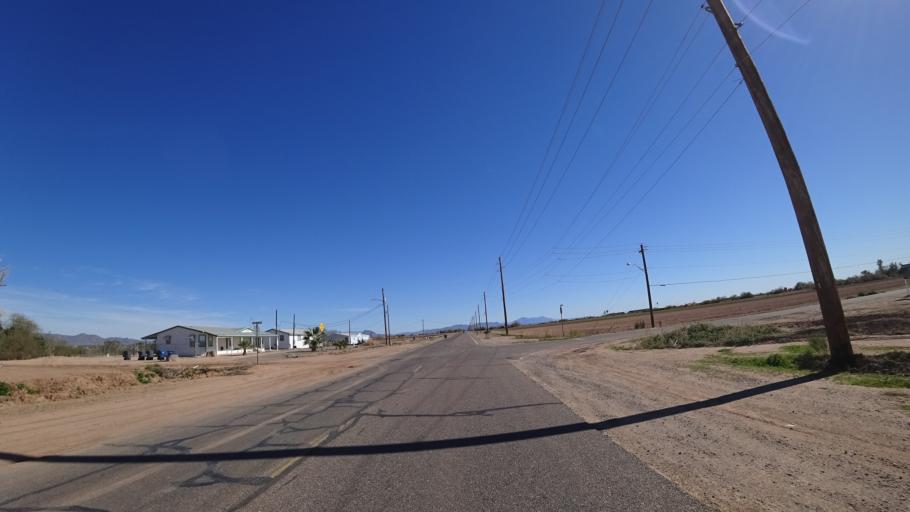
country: US
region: Arizona
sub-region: Maricopa County
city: Scottsdale
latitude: 33.4949
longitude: -111.8832
